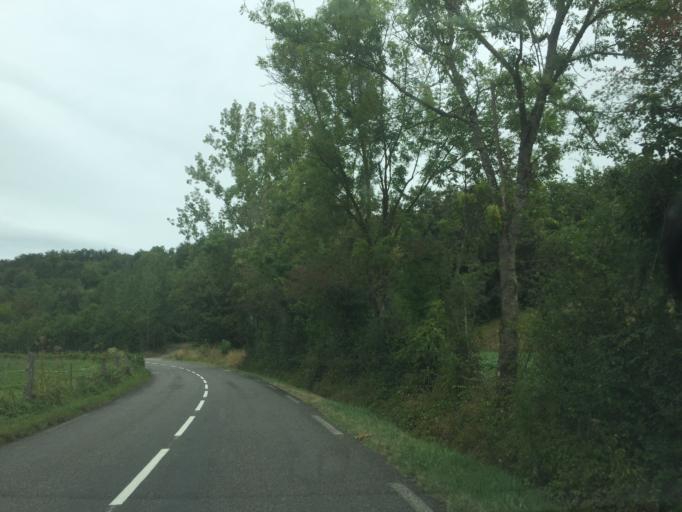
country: FR
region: Midi-Pyrenees
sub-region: Departement des Hautes-Pyrenees
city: Rabastens-de-Bigorre
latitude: 43.3560
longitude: 0.2306
